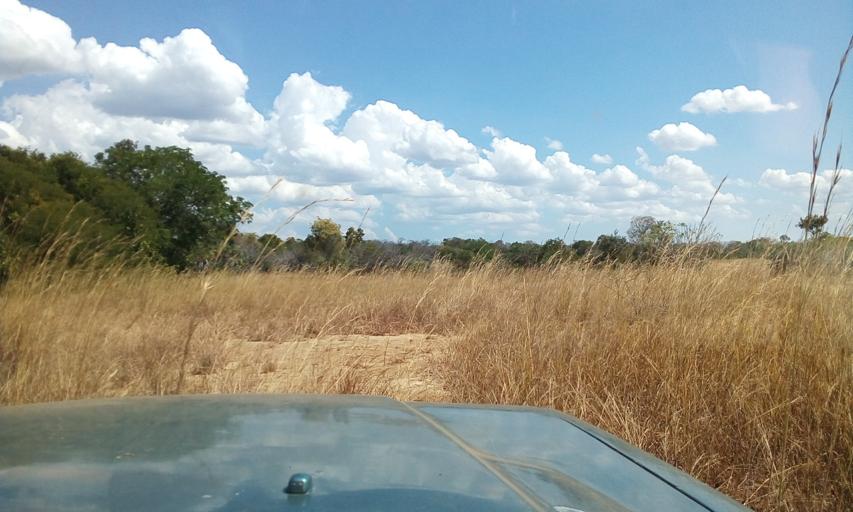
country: MG
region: Melaky
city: Mahabe
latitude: -16.4382
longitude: 45.3753
